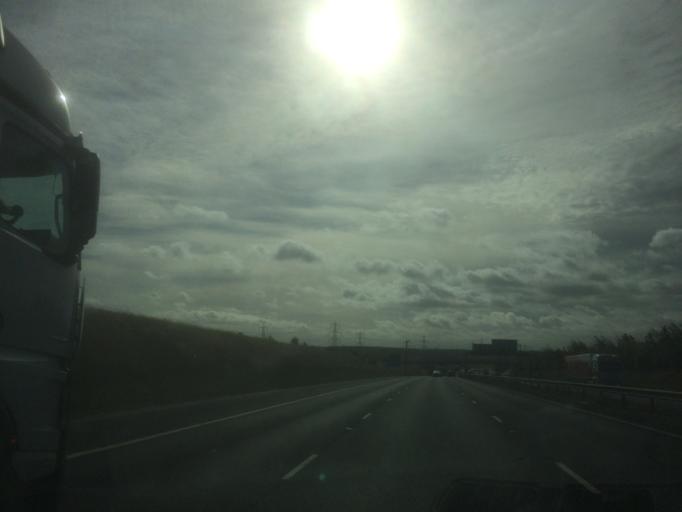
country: GB
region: England
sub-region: North Yorkshire
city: Byram
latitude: 53.7544
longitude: -1.2759
